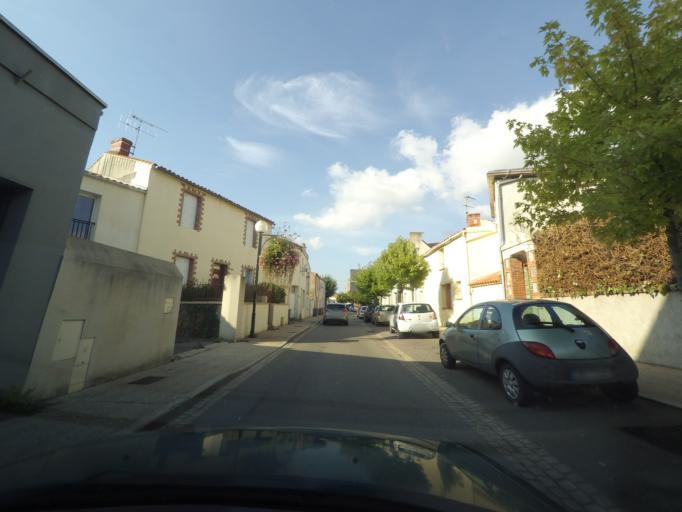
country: FR
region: Pays de la Loire
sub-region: Departement de la Loire-Atlantique
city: Saint-Philbert-de-Grand-Lieu
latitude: 47.0378
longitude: -1.6410
